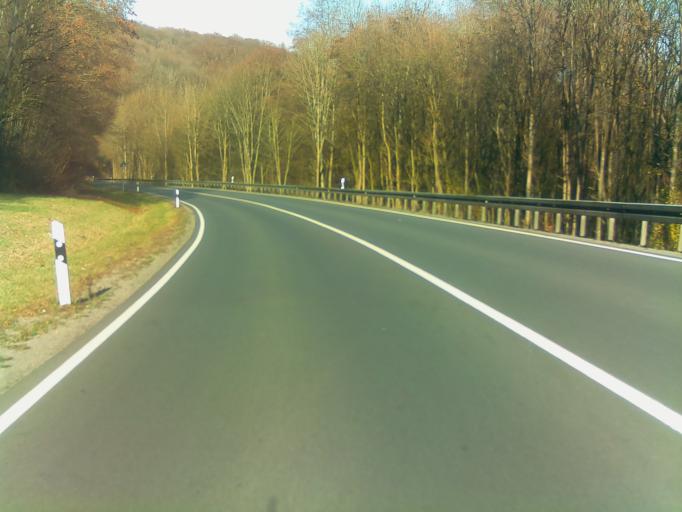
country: DE
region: Bavaria
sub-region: Regierungsbezirk Unterfranken
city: Ramsthal
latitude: 50.1708
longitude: 10.0619
